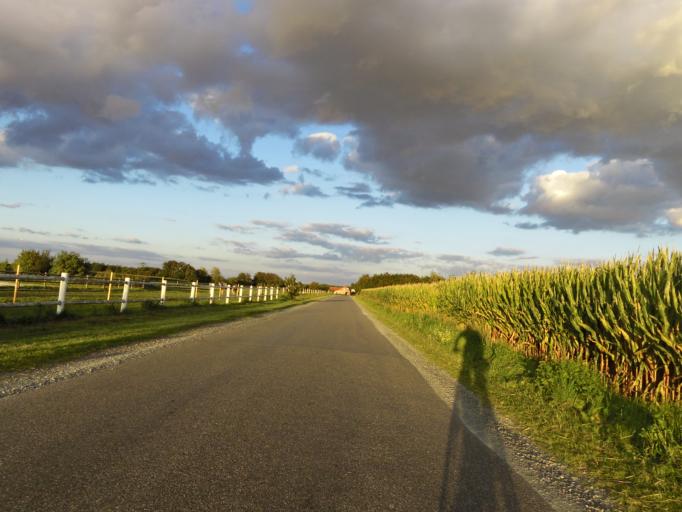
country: DK
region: South Denmark
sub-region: Tonder Kommune
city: Sherrebek
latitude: 55.2389
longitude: 8.8377
